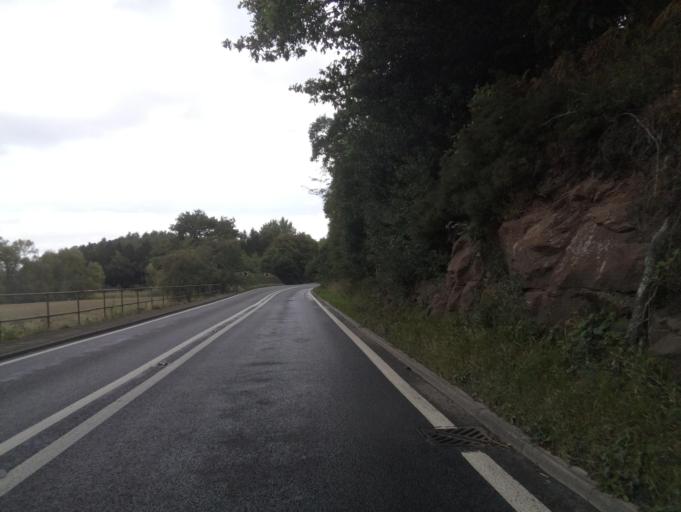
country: GB
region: England
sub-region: Shropshire
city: Bridgnorth
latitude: 52.5534
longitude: -2.4053
